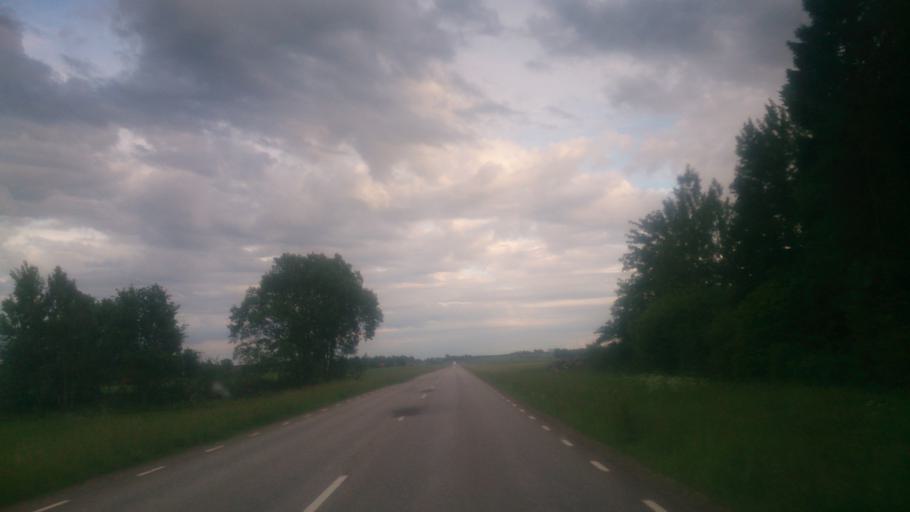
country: SE
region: OEstergoetland
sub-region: Motala Kommun
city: Borensberg
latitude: 58.4963
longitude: 15.2062
